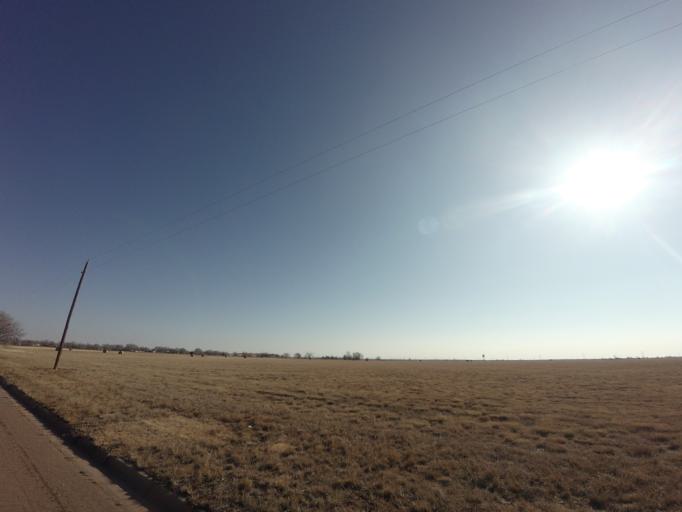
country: US
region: New Mexico
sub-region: Curry County
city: Clovis
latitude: 34.3830
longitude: -103.1912
